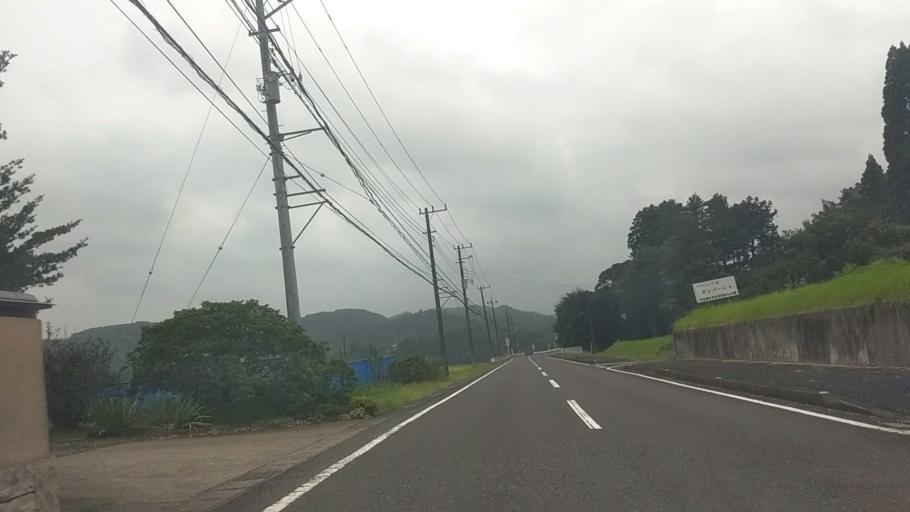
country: JP
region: Chiba
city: Kawaguchi
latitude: 35.2595
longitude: 140.0530
